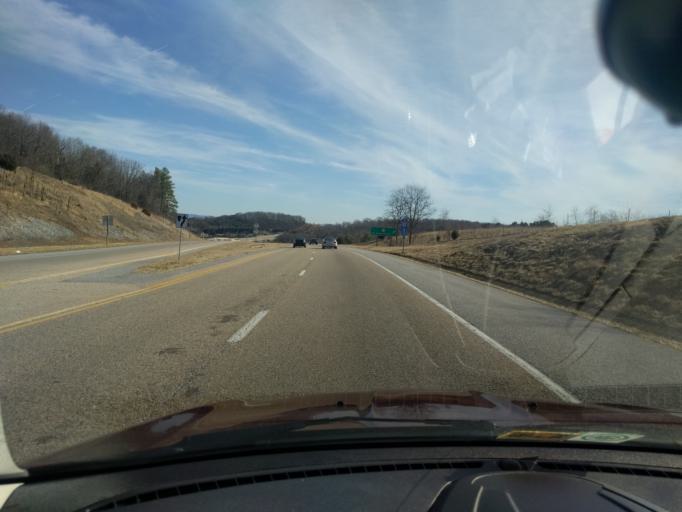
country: US
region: Virginia
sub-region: Augusta County
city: Jolivue
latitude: 38.1261
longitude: -79.0847
